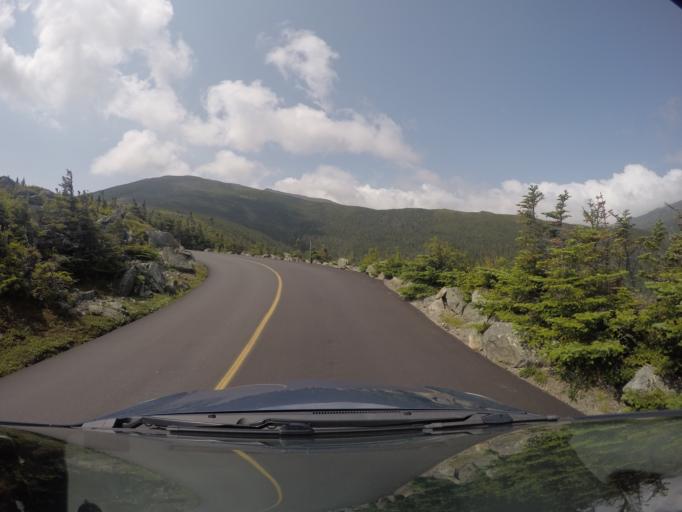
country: US
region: New Hampshire
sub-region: Coos County
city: Gorham
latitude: 44.2954
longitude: -71.2806
